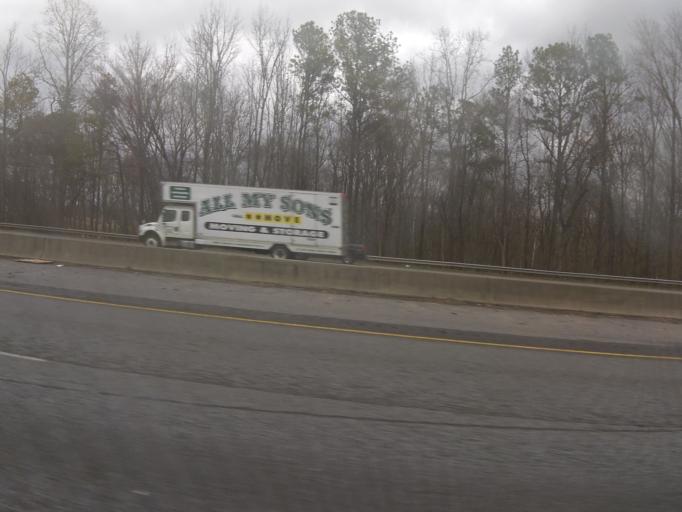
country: US
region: Georgia
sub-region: Whitfield County
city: Dalton
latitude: 34.6665
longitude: -84.9930
